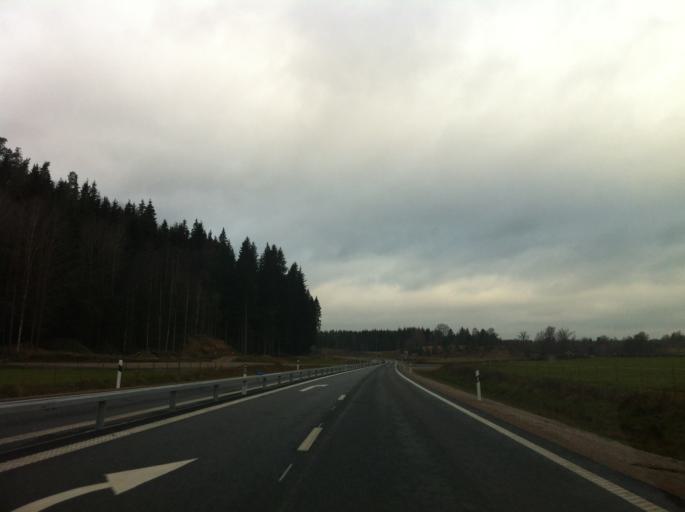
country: SE
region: Joenkoeping
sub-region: Vetlanda Kommun
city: Vetlanda
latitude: 57.4143
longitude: 15.2536
